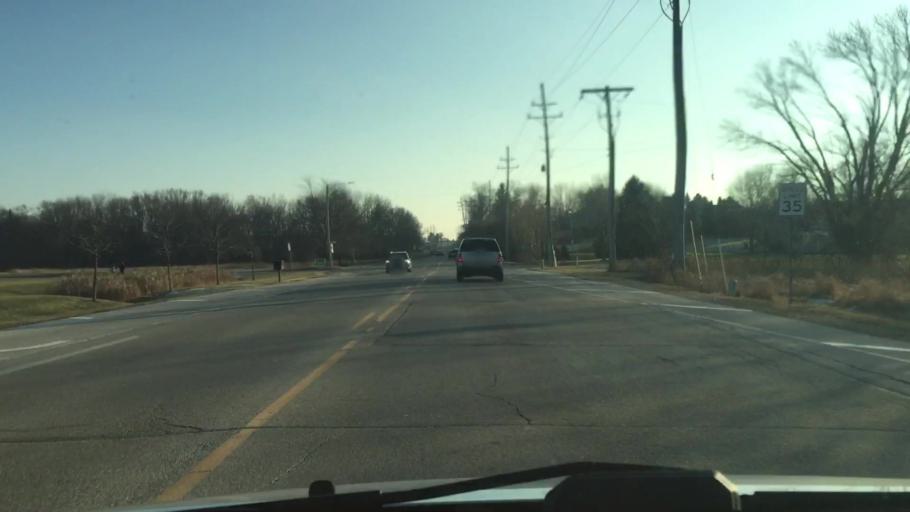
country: US
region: Wisconsin
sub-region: Waukesha County
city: Oconomowoc
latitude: 43.0971
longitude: -88.4958
